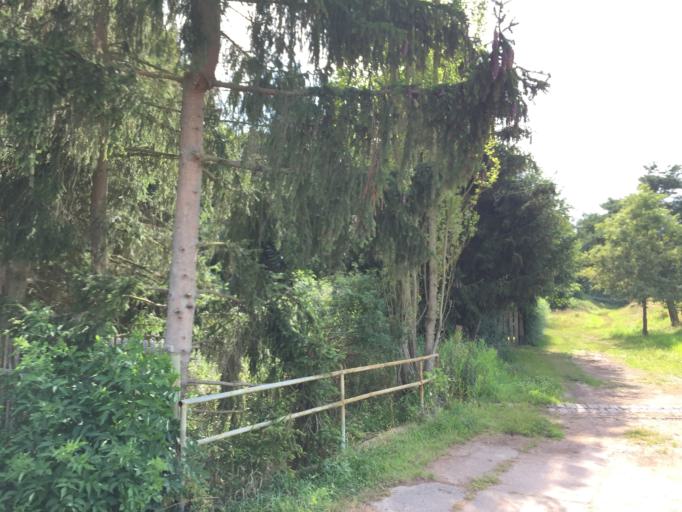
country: DE
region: Thuringia
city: Immelborn
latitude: 50.7841
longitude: 10.2668
